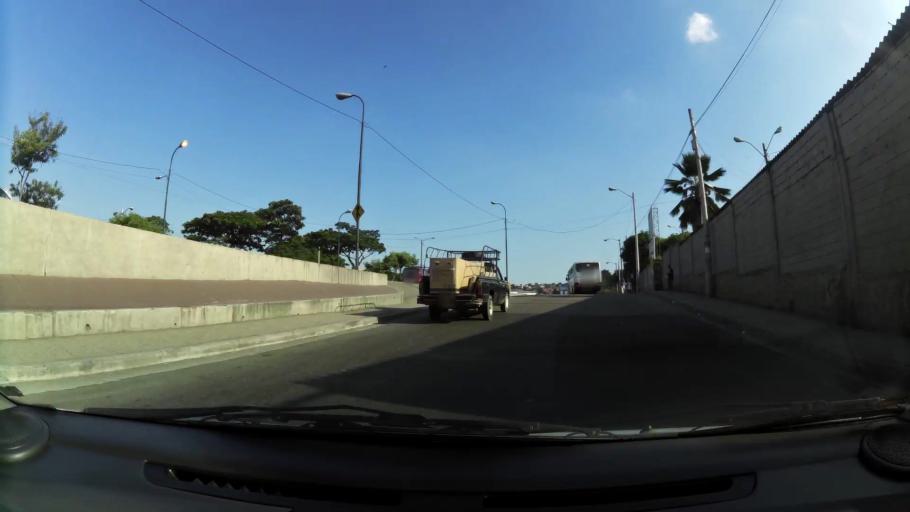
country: EC
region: Guayas
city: Guayaquil
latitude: -2.1477
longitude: -79.9118
